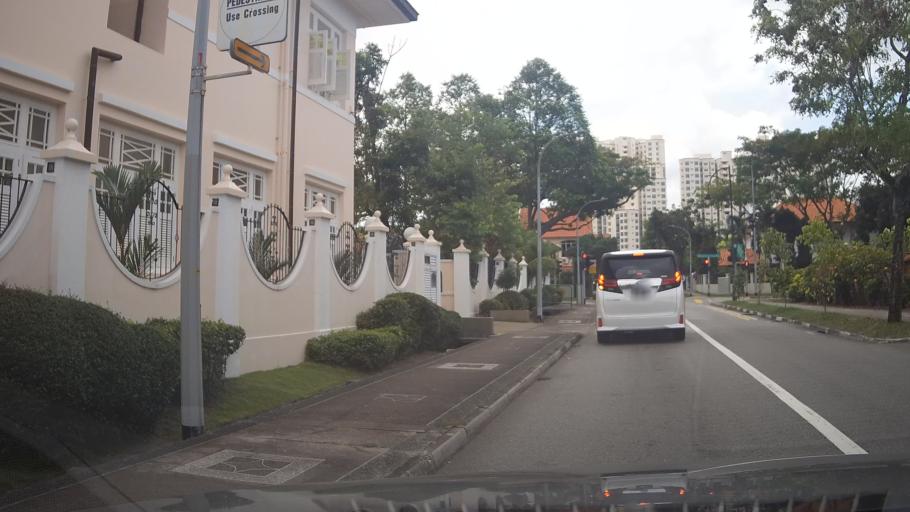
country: SG
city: Singapore
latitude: 1.3015
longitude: 103.8937
